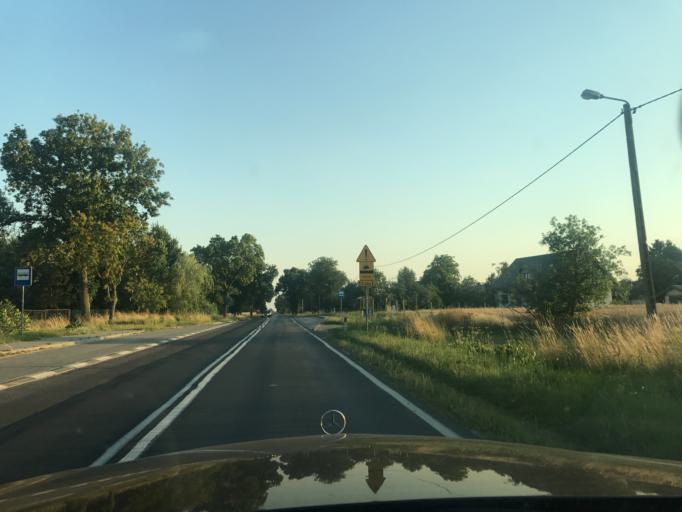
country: PL
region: Lublin Voivodeship
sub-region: Powiat lubartowski
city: Lubartow
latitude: 51.4964
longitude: 22.6372
